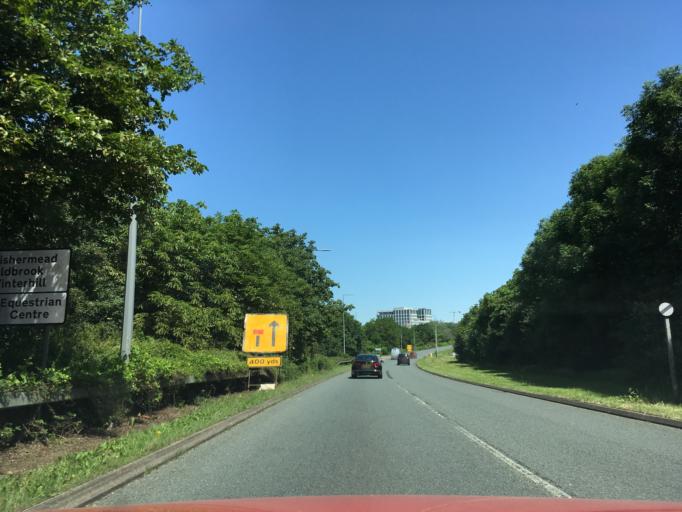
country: GB
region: England
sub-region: Milton Keynes
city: Loughton
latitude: 52.0268
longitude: -0.7751
